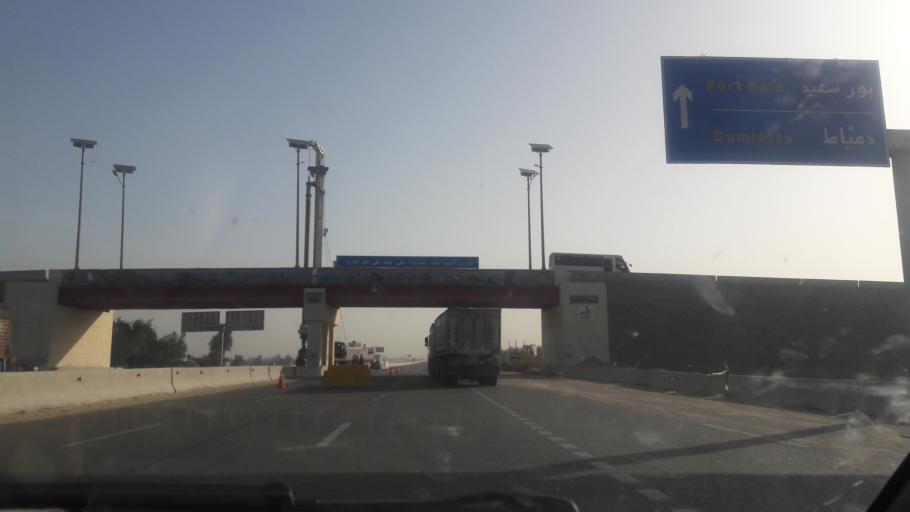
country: EG
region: Al Isma'iliyah
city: Ismailia
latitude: 30.6976
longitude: 32.1081
